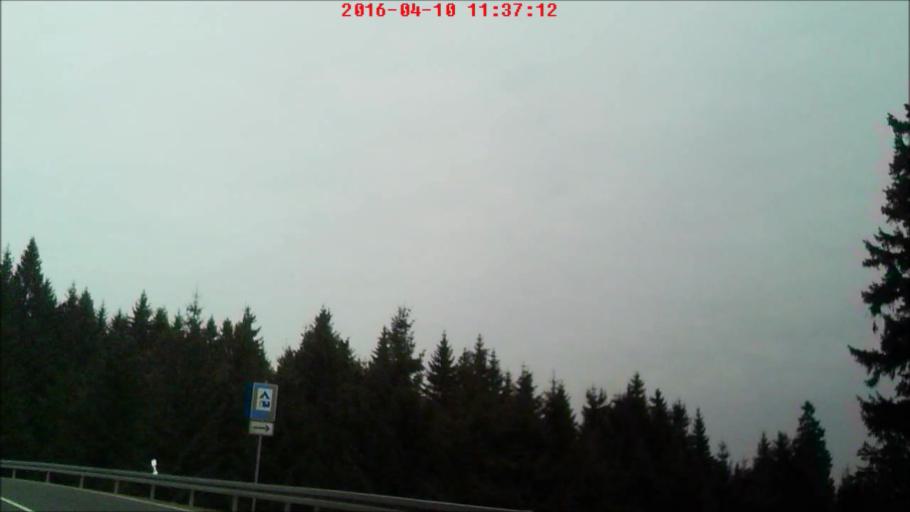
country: DE
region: Thuringia
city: Oberhof
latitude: 50.6953
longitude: 10.7222
